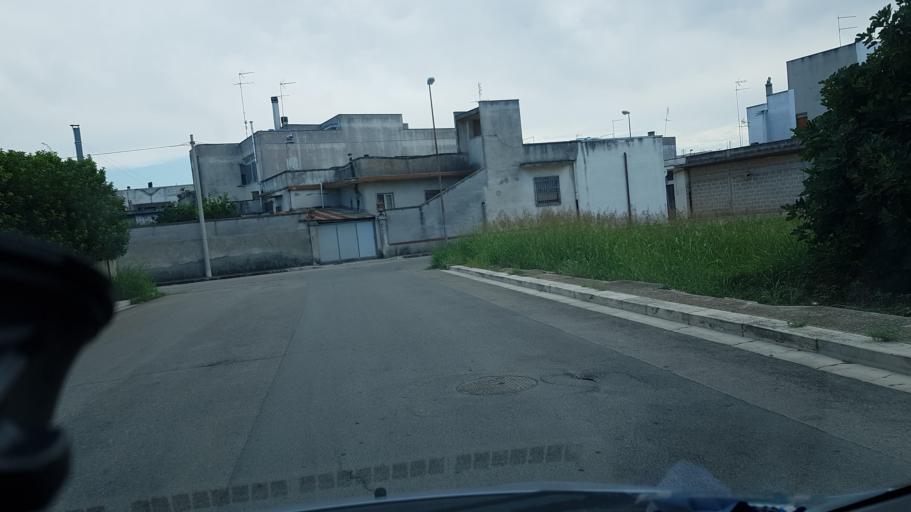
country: IT
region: Apulia
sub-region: Provincia di Brindisi
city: Mesagne
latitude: 40.5649
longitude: 17.8165
